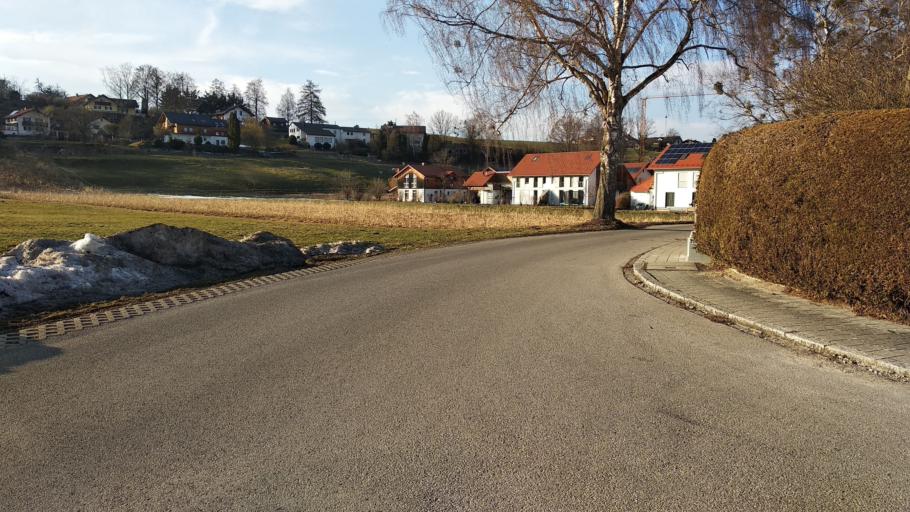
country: DE
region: Bavaria
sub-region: Upper Bavaria
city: Glonn
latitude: 47.9832
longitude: 11.8623
